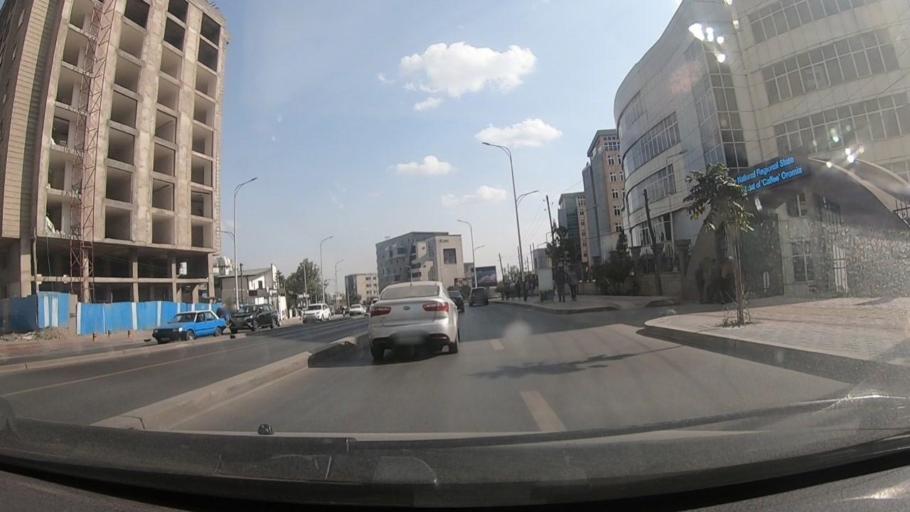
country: ET
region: Adis Abeba
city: Addis Ababa
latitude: 8.9921
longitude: 38.7395
